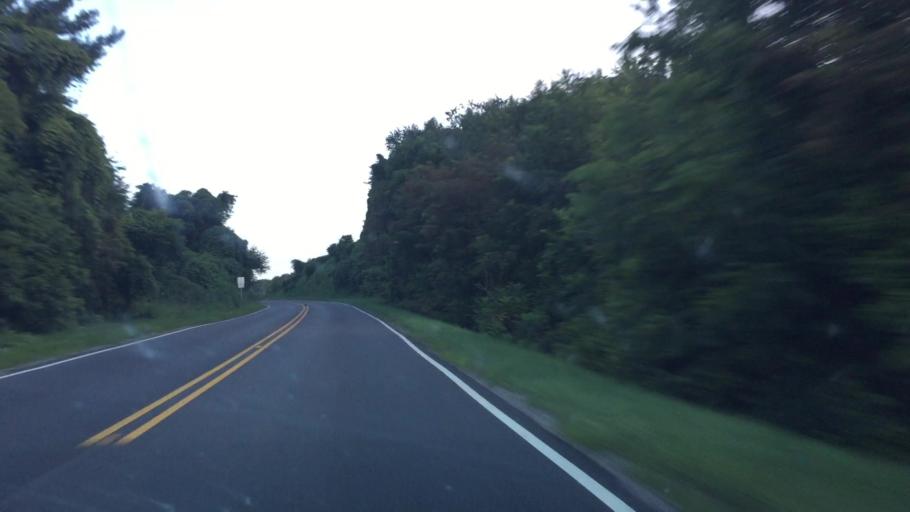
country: US
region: Virginia
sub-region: Wythe County
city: Wytheville
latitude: 36.9361
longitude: -80.9445
